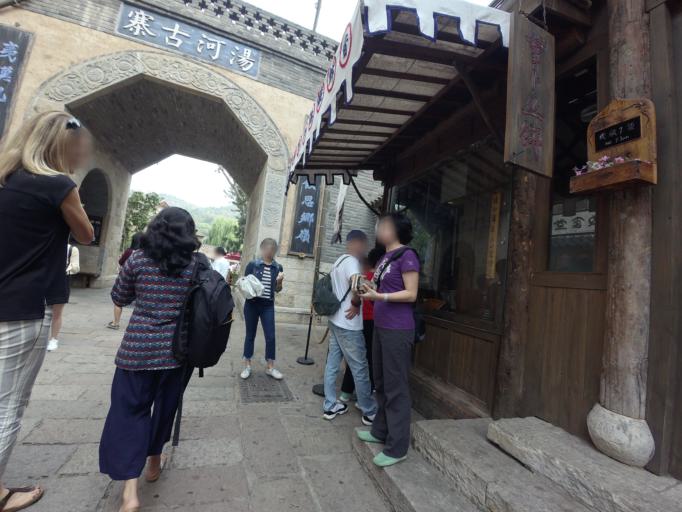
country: CN
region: Beijing
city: Xinchengzi
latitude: 40.6508
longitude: 117.2690
